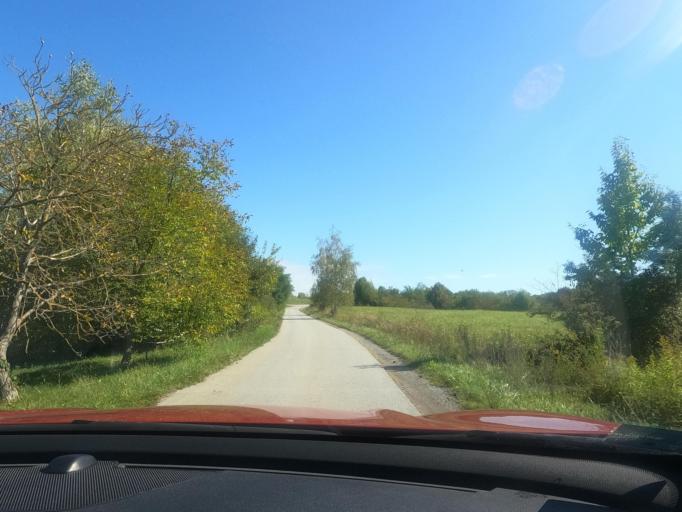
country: HR
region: Sisacko-Moslavacka
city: Petrinja
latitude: 45.4235
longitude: 16.2569
